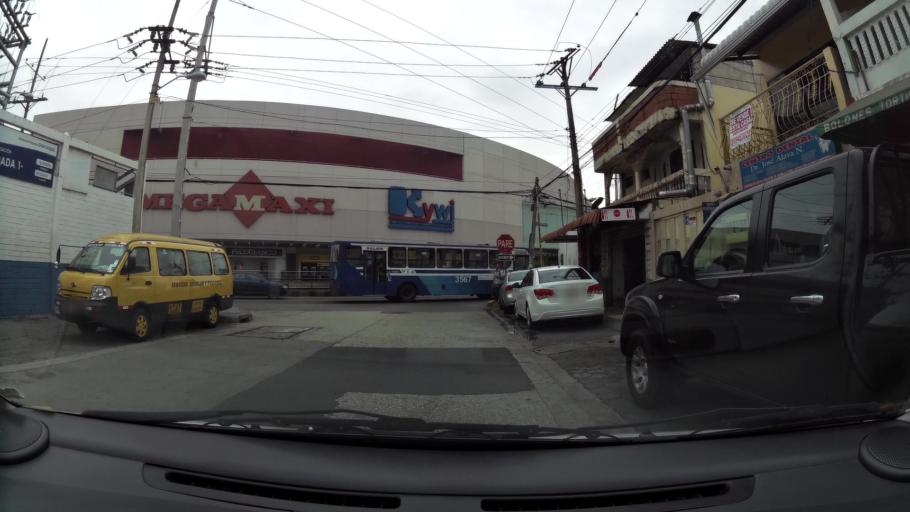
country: EC
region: Guayas
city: Eloy Alfaro
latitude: -2.1416
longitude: -79.9086
